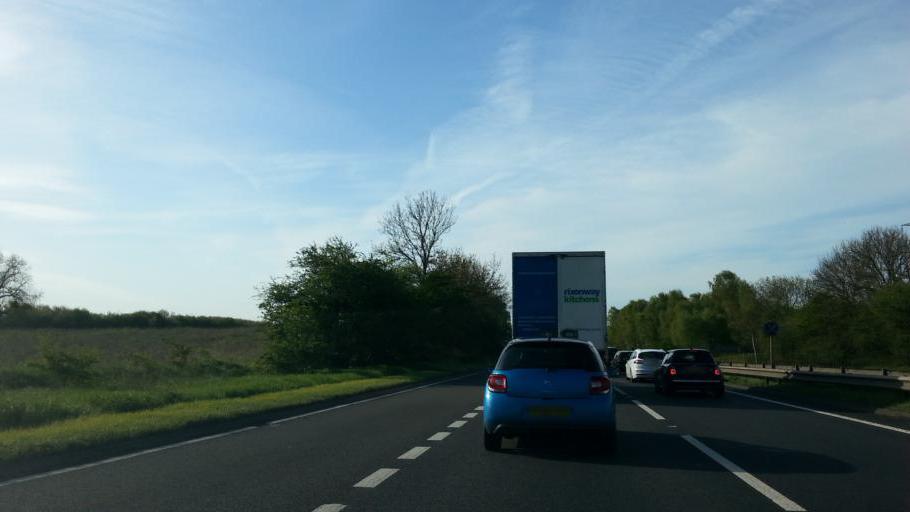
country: GB
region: England
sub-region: Lincolnshire
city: Barrowby
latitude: 52.9155
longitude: -0.6796
